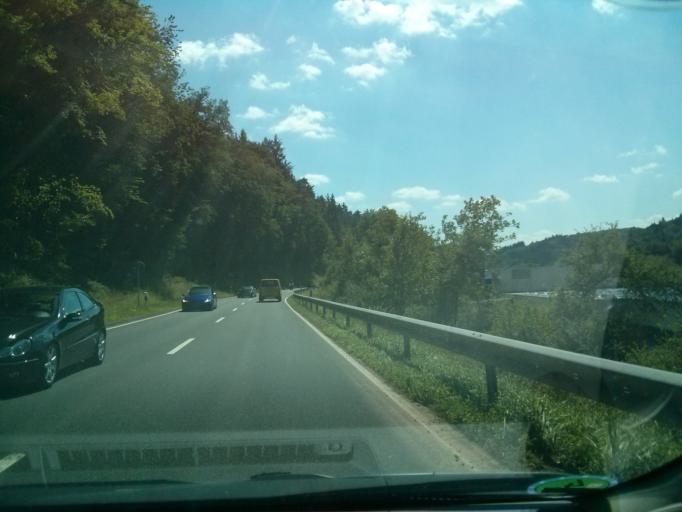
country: DE
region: Rheinland-Pfalz
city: Leimbach
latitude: 50.4083
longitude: 6.9311
